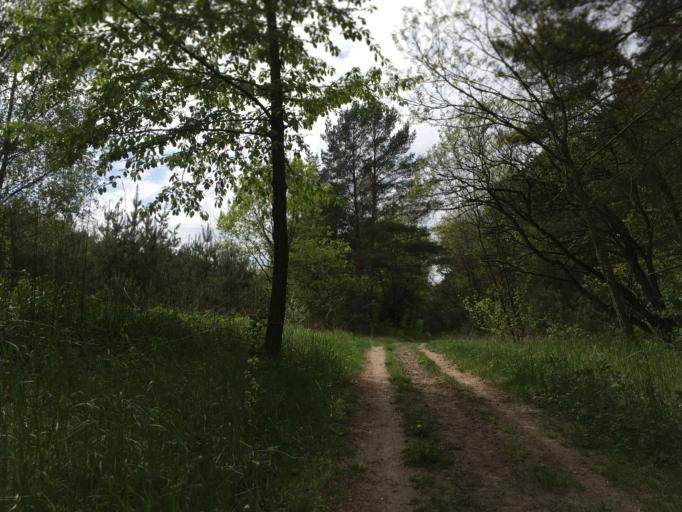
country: DE
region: Brandenburg
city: Rudnitz
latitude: 52.7094
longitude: 13.6273
